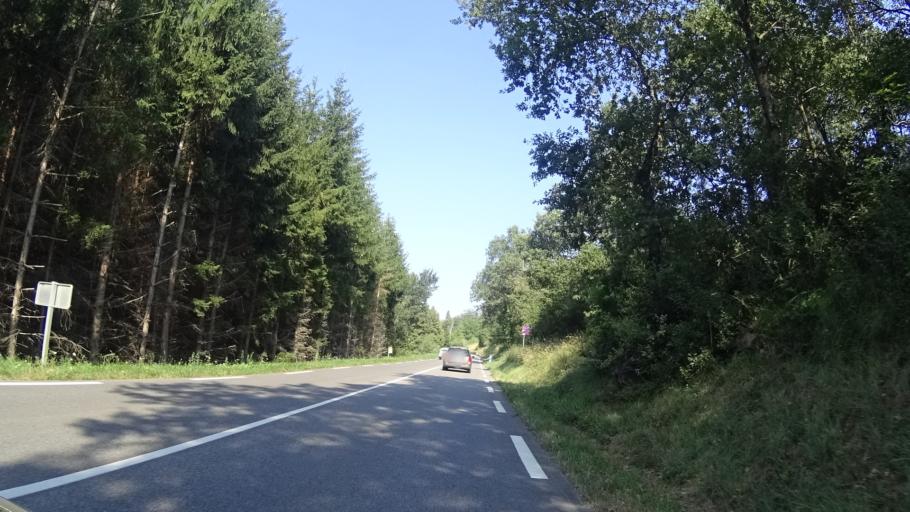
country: FR
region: Midi-Pyrenees
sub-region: Departement de l'Ariege
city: Lavelanet
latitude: 42.9218
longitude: 1.8806
